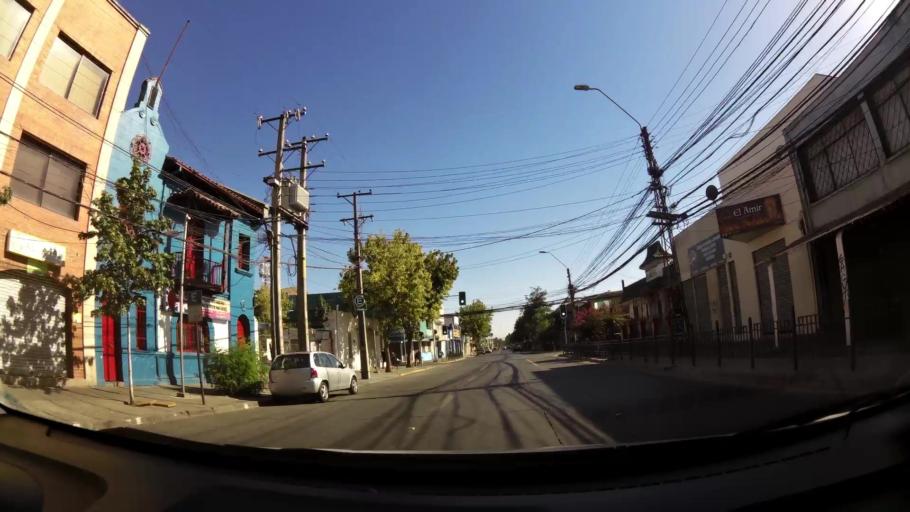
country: CL
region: O'Higgins
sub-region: Provincia de Cachapoal
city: Rancagua
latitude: -34.1711
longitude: -70.7466
